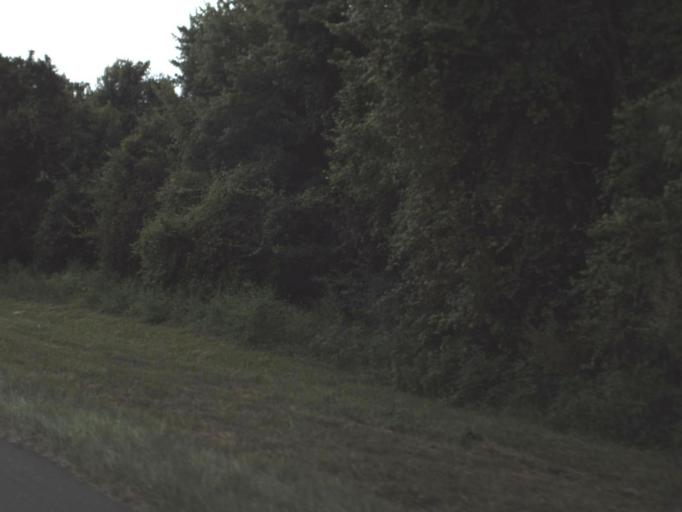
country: US
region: Florida
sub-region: Hillsborough County
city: Plant City
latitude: 28.0240
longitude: -82.0747
